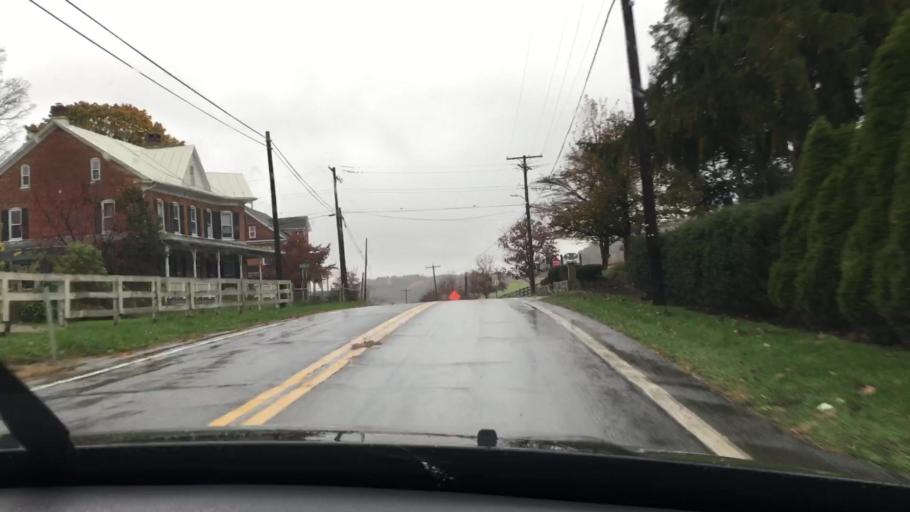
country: US
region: Maryland
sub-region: Carroll County
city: Manchester
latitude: 39.7162
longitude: -76.8490
